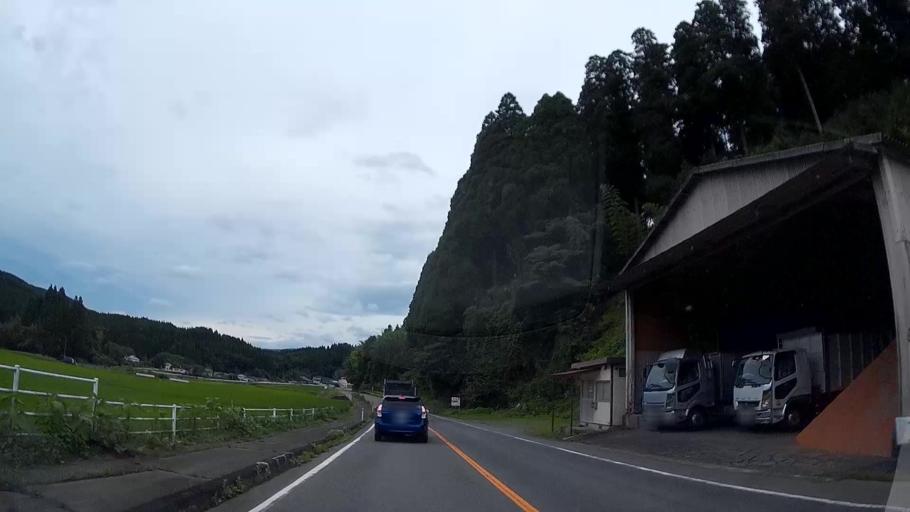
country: JP
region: Kumamoto
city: Aso
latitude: 33.1253
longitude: 131.0316
